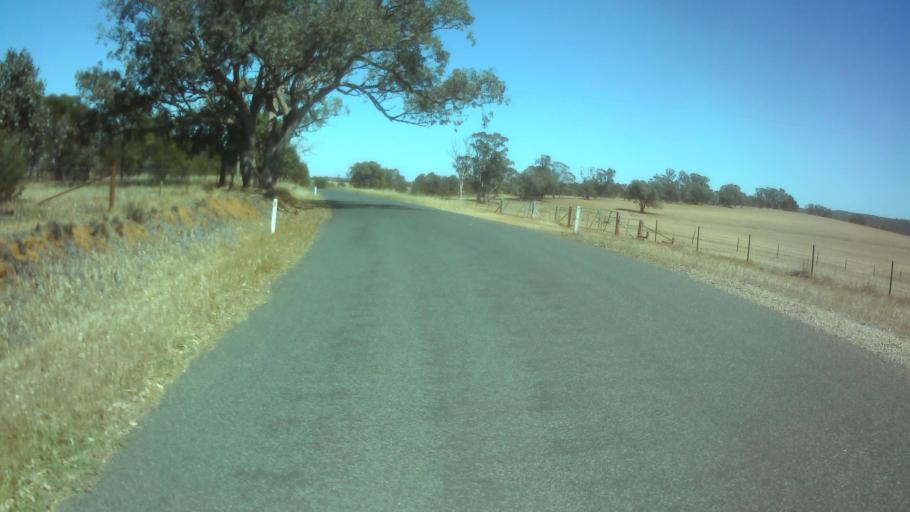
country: AU
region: New South Wales
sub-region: Weddin
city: Grenfell
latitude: -33.9467
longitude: 148.3920
